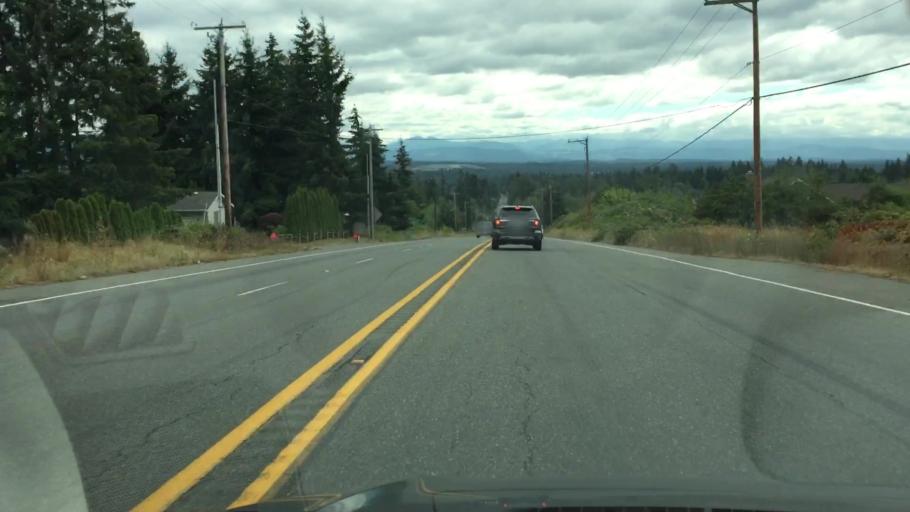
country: US
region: Washington
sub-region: Pierce County
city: Graham
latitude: 47.0265
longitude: -122.2961
